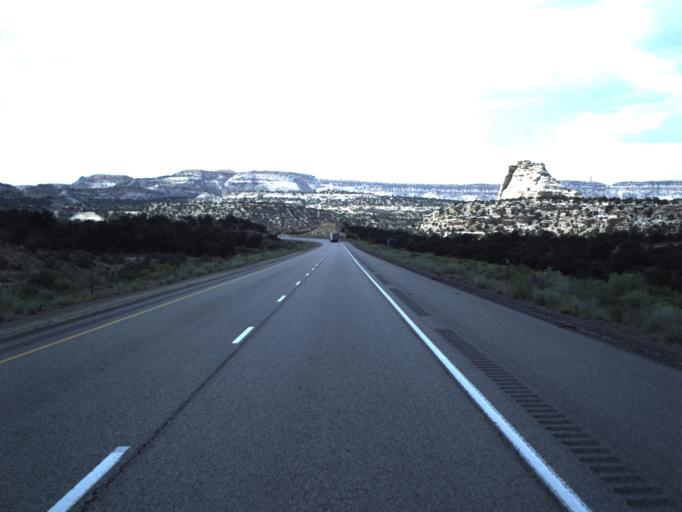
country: US
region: Utah
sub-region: Emery County
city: Ferron
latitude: 38.8637
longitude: -110.8574
